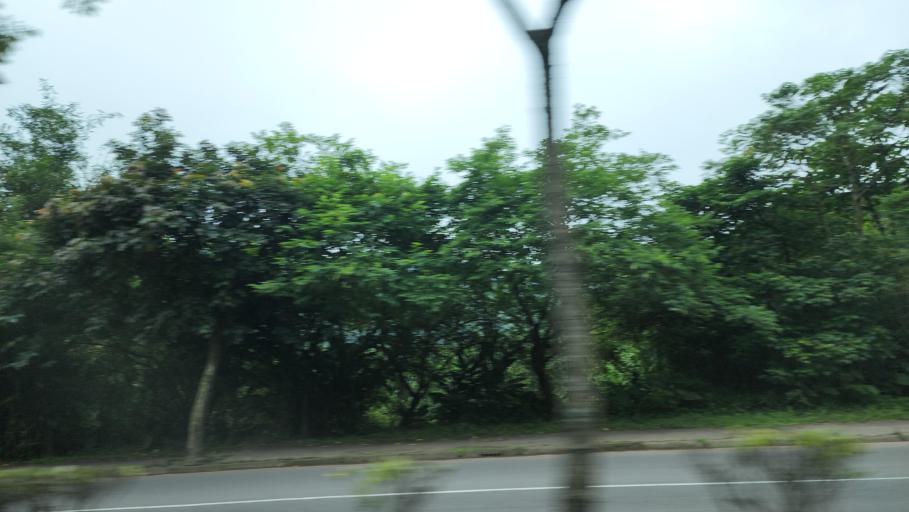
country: TW
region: Taiwan
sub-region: Keelung
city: Keelung
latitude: 25.1615
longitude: 121.6897
